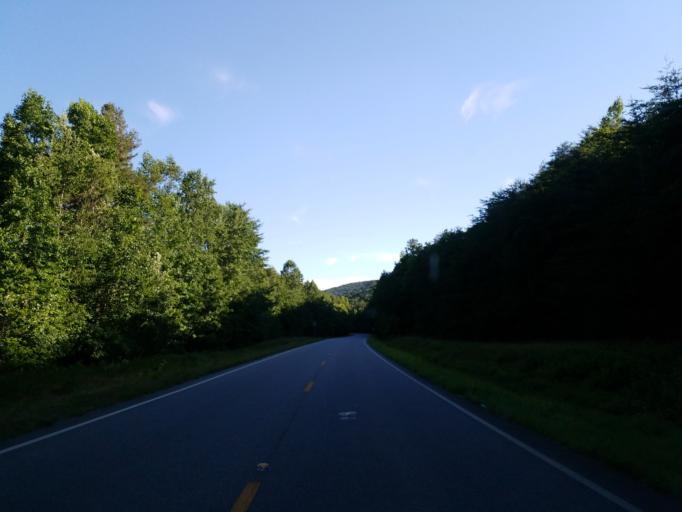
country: US
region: Georgia
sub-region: Whitfield County
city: Dalton
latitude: 34.6556
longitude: -85.0597
